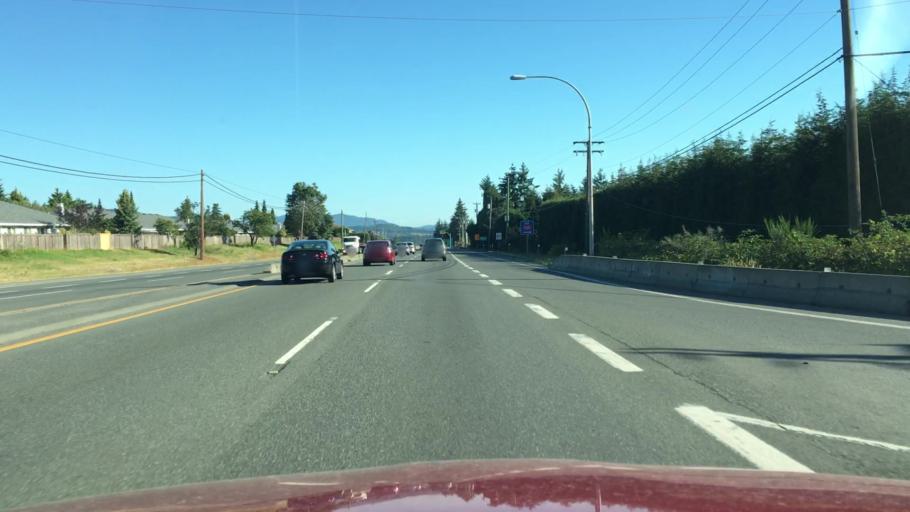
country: CA
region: British Columbia
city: North Saanich
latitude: 48.5544
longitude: -123.3928
